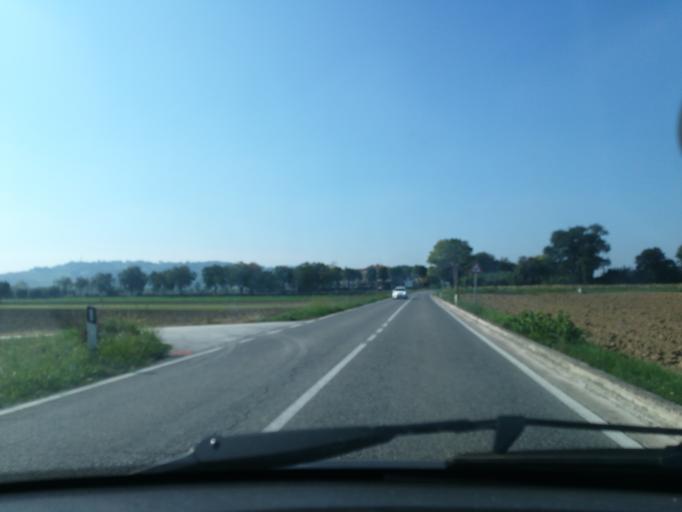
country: IT
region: The Marches
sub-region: Provincia di Macerata
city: Zona Industriale
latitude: 43.2661
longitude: 13.4589
